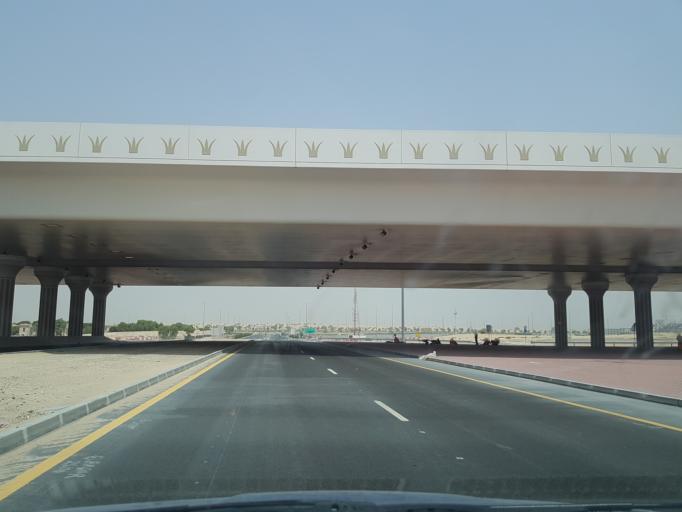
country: AE
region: Dubai
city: Dubai
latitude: 25.0579
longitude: 55.3016
